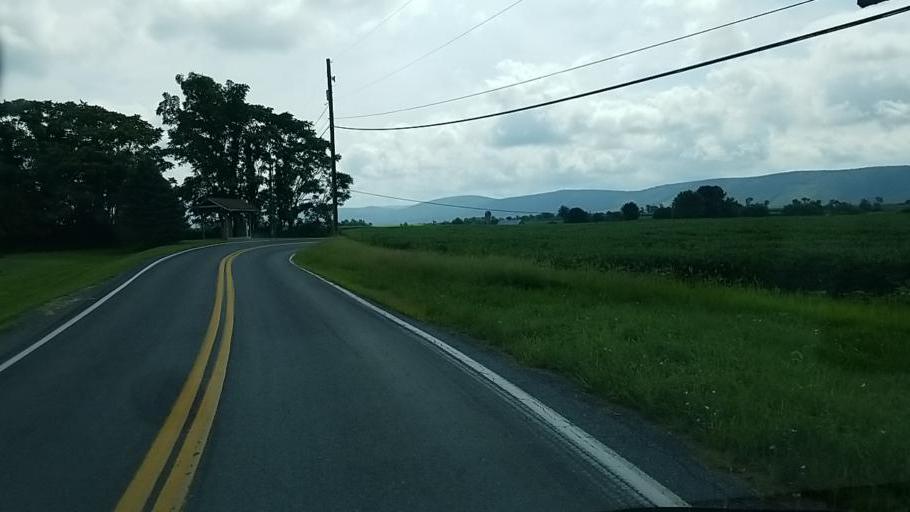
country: US
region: Pennsylvania
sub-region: Dauphin County
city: Millersburg
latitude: 40.5637
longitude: -76.8950
